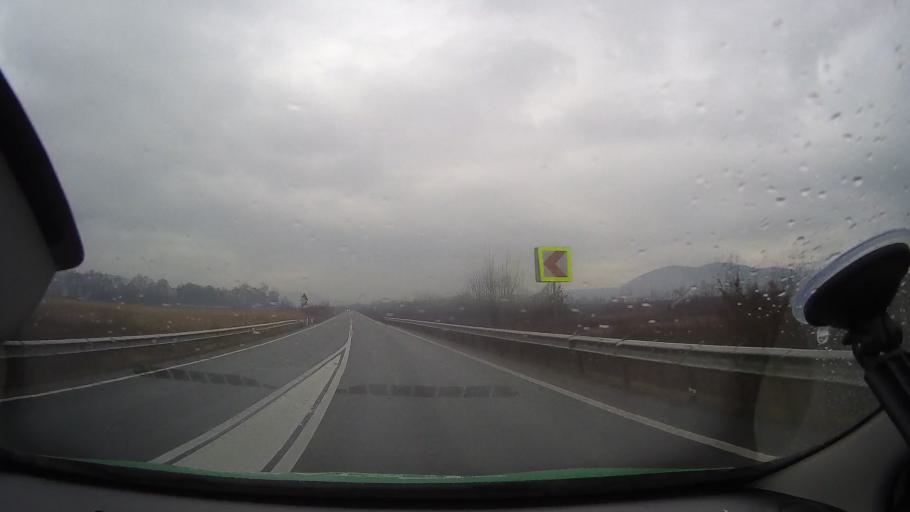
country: RO
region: Hunedoara
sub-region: Comuna Tomesti
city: Tomesti
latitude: 46.1801
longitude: 22.6632
